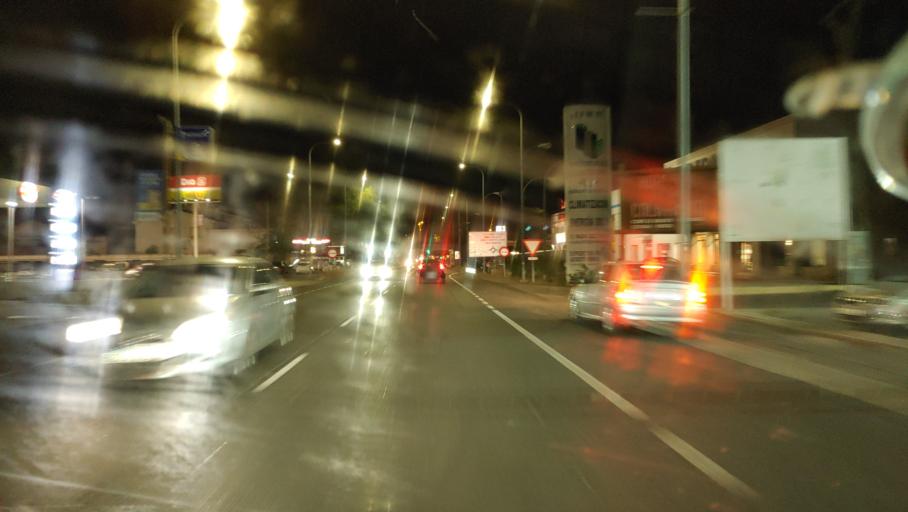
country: ES
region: Castille-La Mancha
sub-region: Provincia de Ciudad Real
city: Ciudad Real
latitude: 38.9882
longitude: -3.9123
